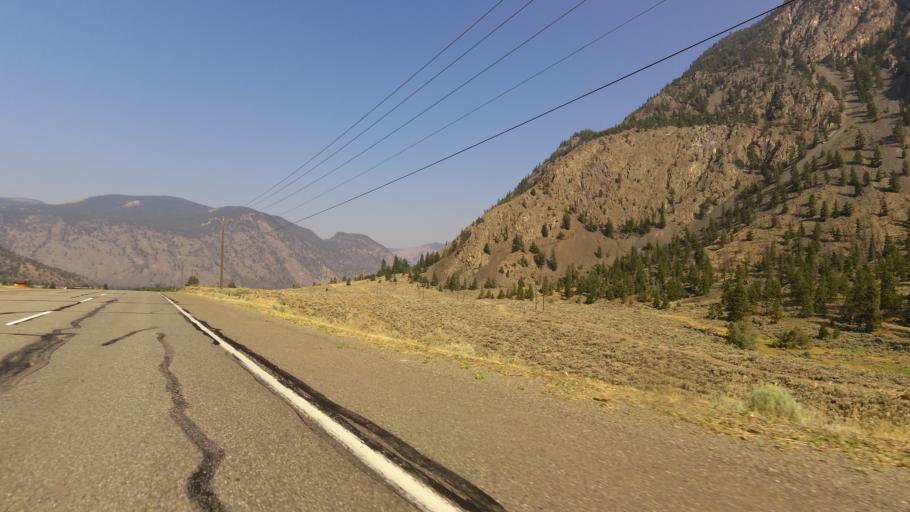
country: CA
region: British Columbia
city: Oliver
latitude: 49.2205
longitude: -119.9445
